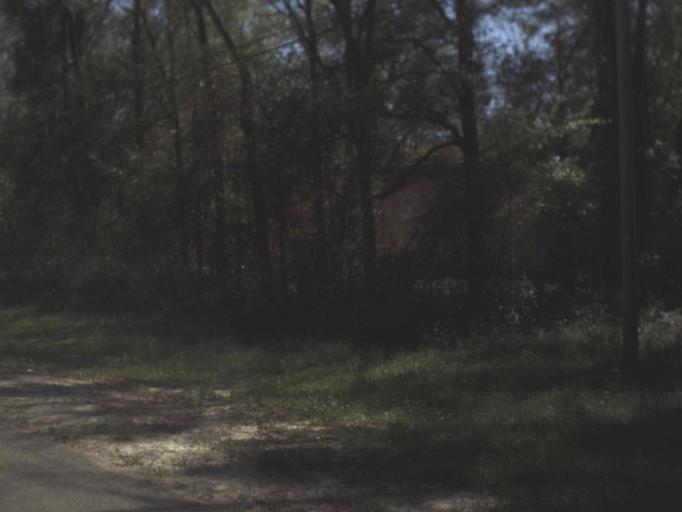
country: US
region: Florida
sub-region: Leon County
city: Tallahassee
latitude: 30.3771
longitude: -84.2992
